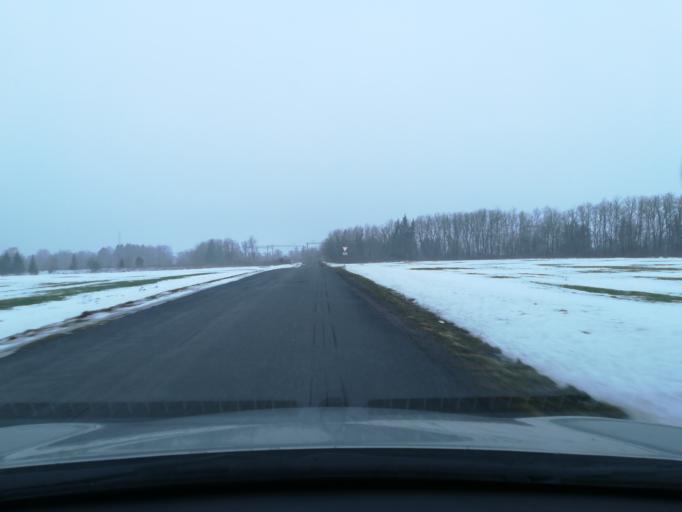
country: EE
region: Harju
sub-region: Raasiku vald
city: Raasiku
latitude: 59.3625
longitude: 25.1910
